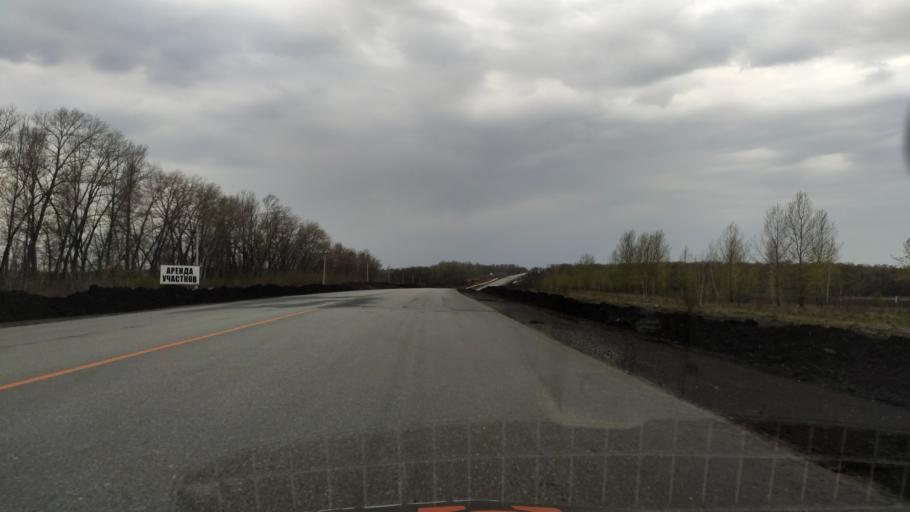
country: RU
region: Kursk
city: Gorshechnoye
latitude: 51.5476
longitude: 38.0585
